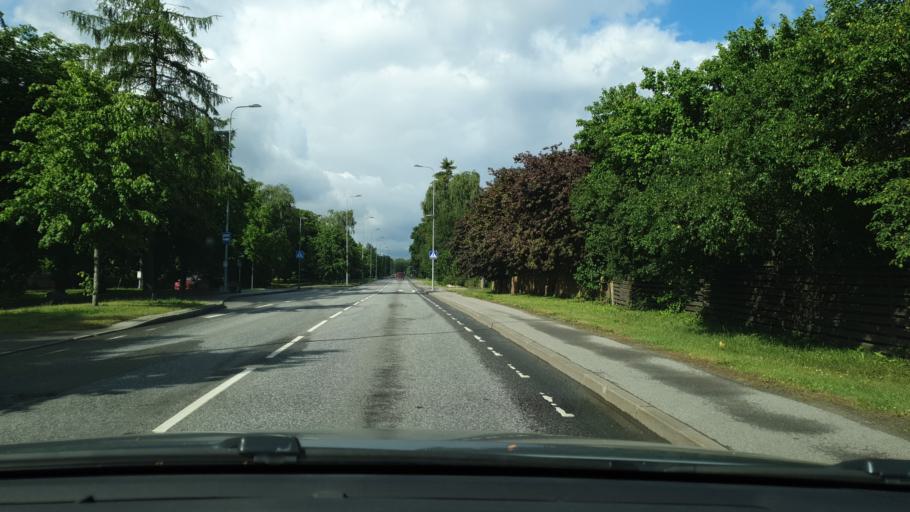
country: EE
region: Harju
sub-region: Viimsi vald
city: Viimsi
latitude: 59.4900
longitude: 24.8765
